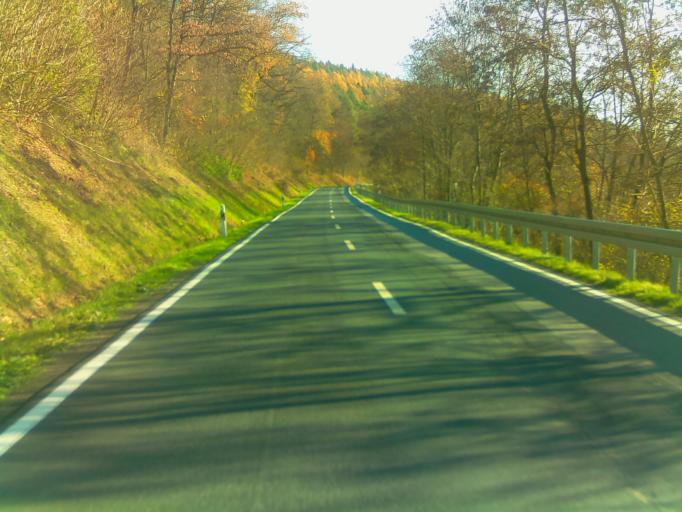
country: DE
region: Bavaria
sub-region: Regierungsbezirk Unterfranken
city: Niederlauer
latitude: 50.2982
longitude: 10.1445
